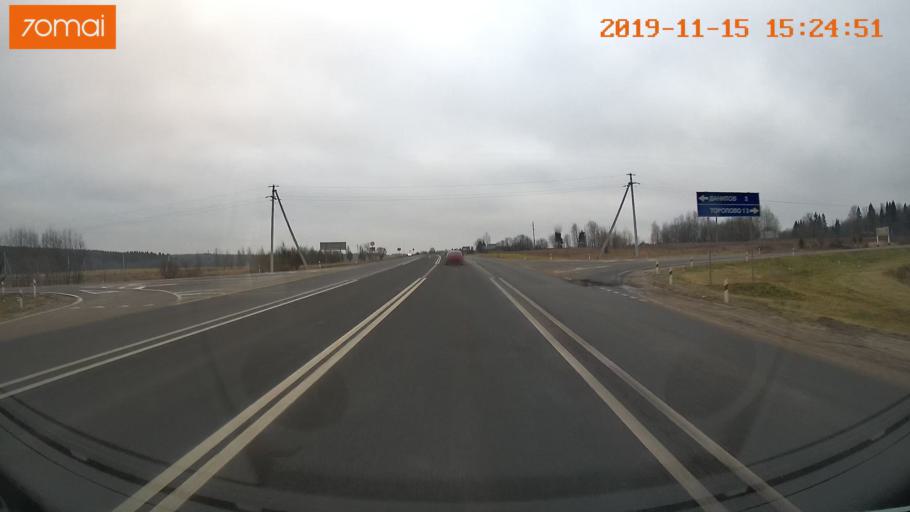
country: RU
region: Jaroslavl
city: Danilov
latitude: 58.1719
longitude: 40.1340
